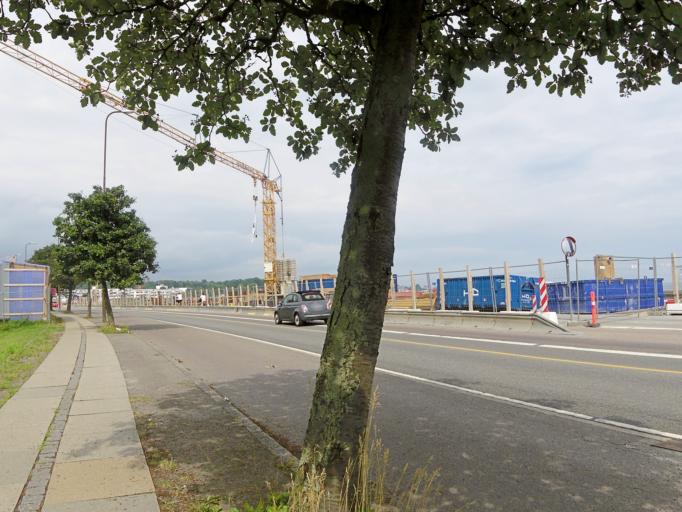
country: DK
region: Capital Region
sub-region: Gentofte Kommune
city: Charlottenlund
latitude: 55.7722
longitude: 12.5954
